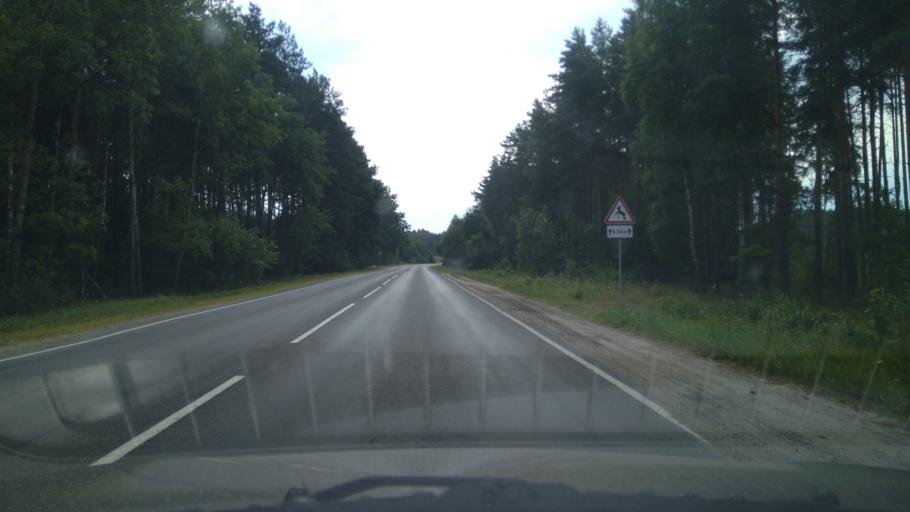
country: BY
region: Brest
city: Nyakhachava
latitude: 52.5871
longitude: 25.0946
